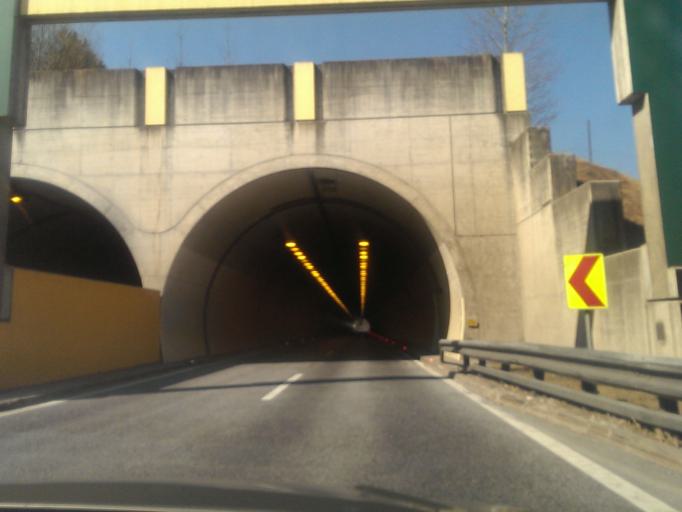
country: AT
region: Upper Austria
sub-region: Politischer Bezirk Kirchdorf an der Krems
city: Rossleithen
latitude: 47.7655
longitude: 14.1939
